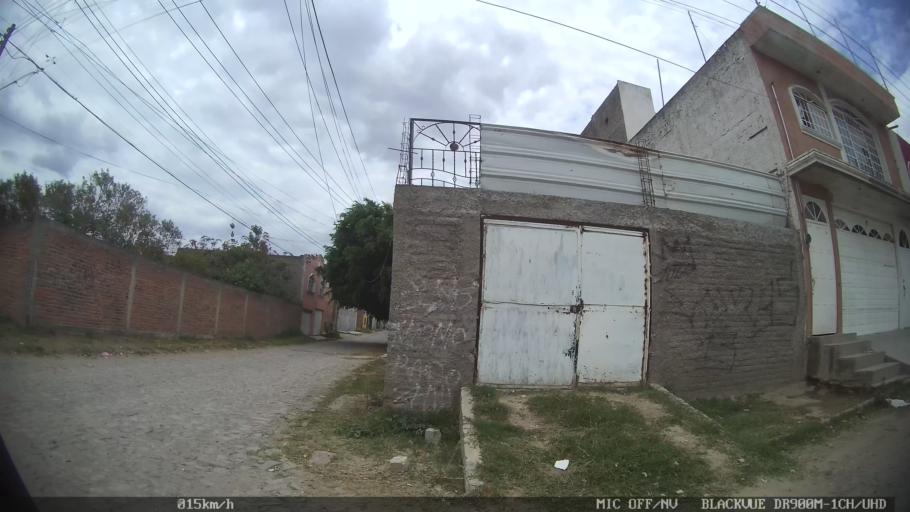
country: MX
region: Jalisco
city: Tonala
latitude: 20.6478
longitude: -103.2548
